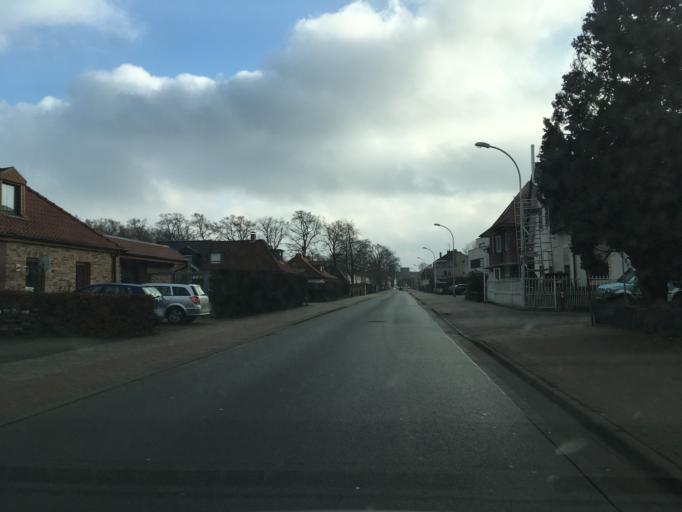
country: DE
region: North Rhine-Westphalia
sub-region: Regierungsbezirk Munster
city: Gronau
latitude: 52.2206
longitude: 7.0150
